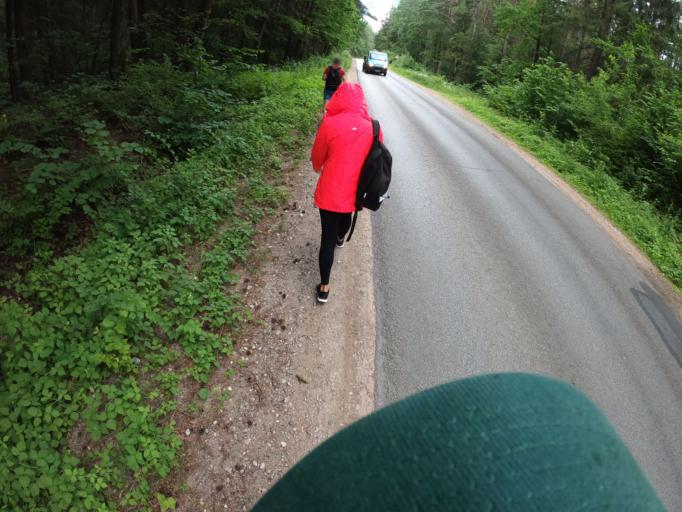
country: LT
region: Alytaus apskritis
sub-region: Alytus
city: Alytus
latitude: 54.4258
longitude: 24.0836
